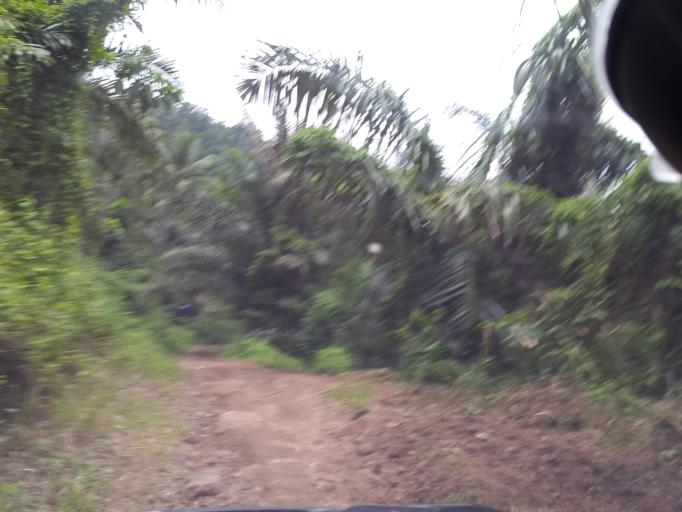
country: ID
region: West Nusa Tenggara
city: Penimbung Barat
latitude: -8.5228
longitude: 116.1259
